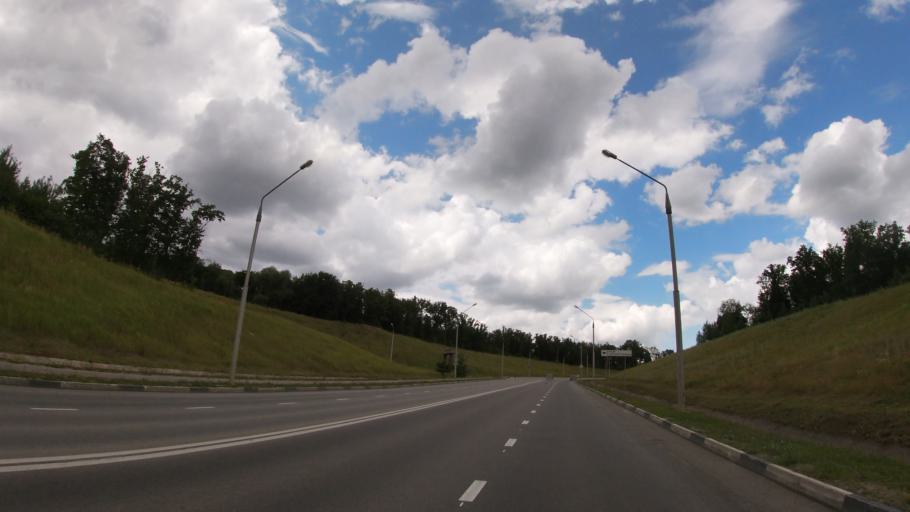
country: RU
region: Belgorod
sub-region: Belgorodskiy Rayon
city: Belgorod
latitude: 50.6221
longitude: 36.6136
